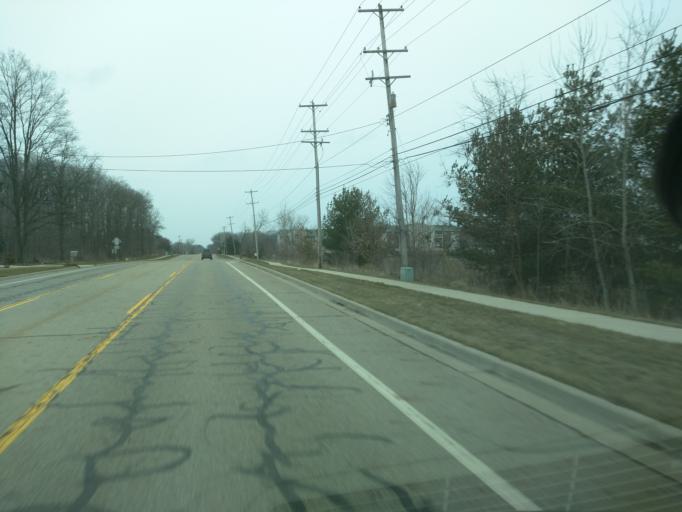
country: US
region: Michigan
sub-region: Eaton County
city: Waverly
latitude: 42.7555
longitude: -84.6602
